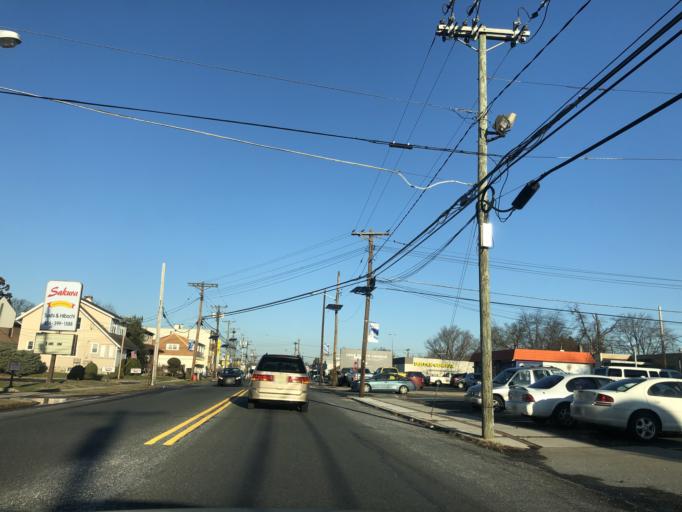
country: US
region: New Jersey
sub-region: Camden County
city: Oaklyn
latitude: 39.9047
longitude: -75.0790
